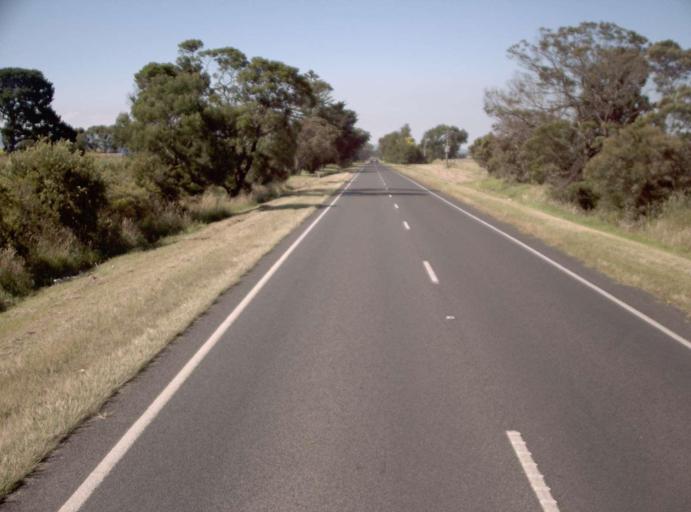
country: AU
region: Victoria
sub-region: Latrobe
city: Traralgon
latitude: -38.5936
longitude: 146.6692
